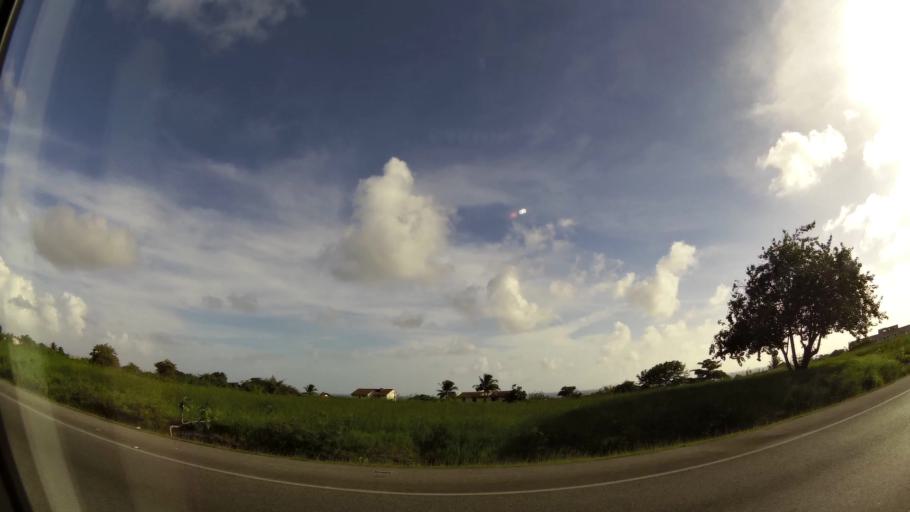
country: BB
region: Christ Church
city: Oistins
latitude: 13.0767
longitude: -59.5644
